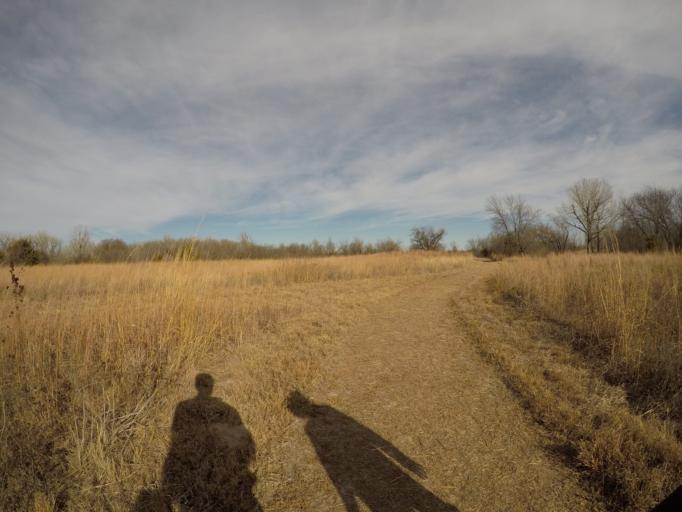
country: US
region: Kansas
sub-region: Reno County
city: Buhler
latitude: 38.1216
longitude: -97.8569
